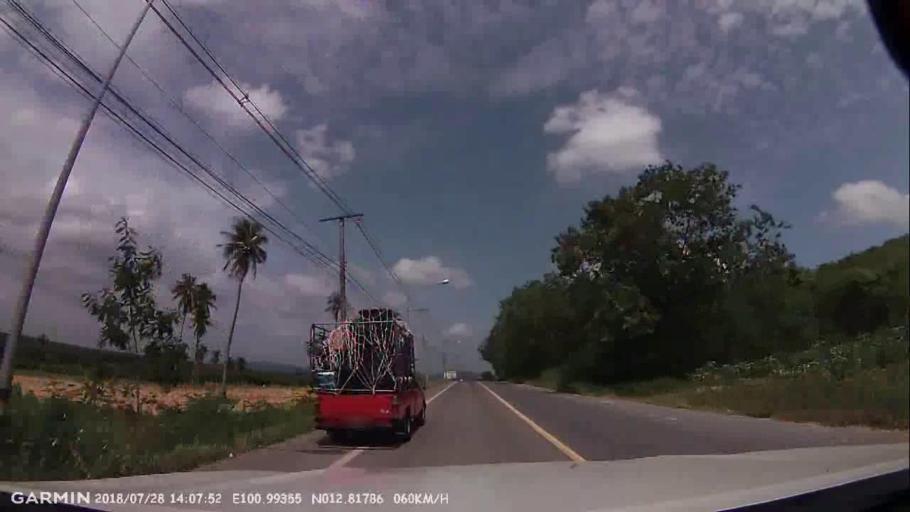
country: TH
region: Rayong
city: Ban Chang
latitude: 12.8178
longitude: 100.9936
